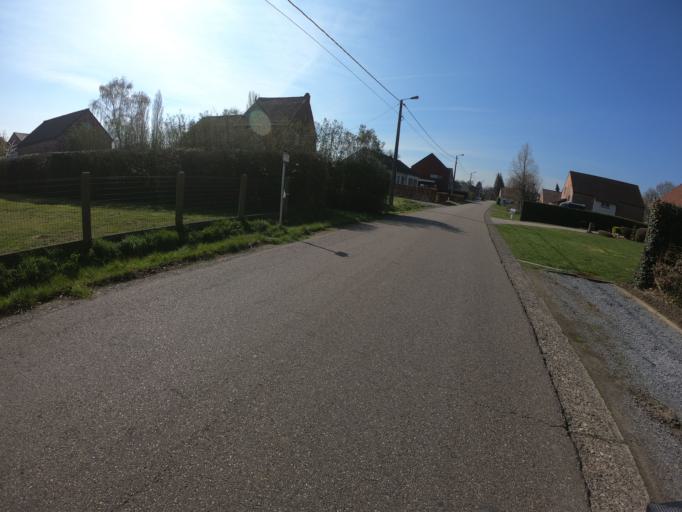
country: BE
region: Flanders
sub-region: Provincie Limburg
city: Herk-de-Stad
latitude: 50.9536
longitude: 5.1943
